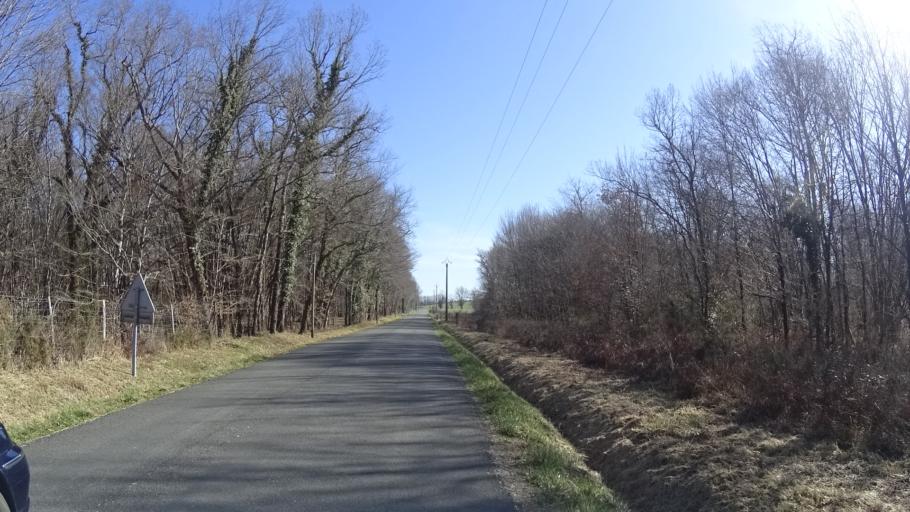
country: FR
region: Aquitaine
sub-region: Departement de la Dordogne
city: Saint-Aulaye
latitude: 45.1281
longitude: 0.2455
